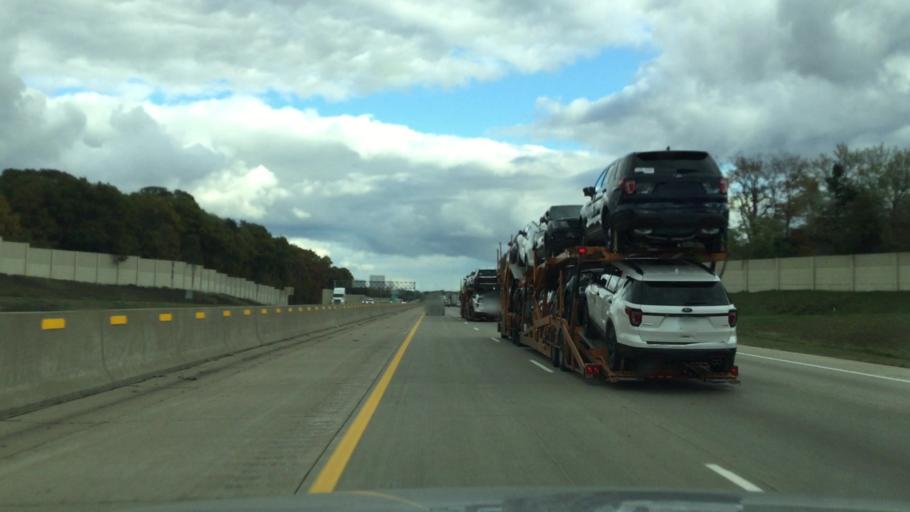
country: US
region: Michigan
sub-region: Kalamazoo County
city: Portage
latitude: 42.2378
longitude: -85.6127
